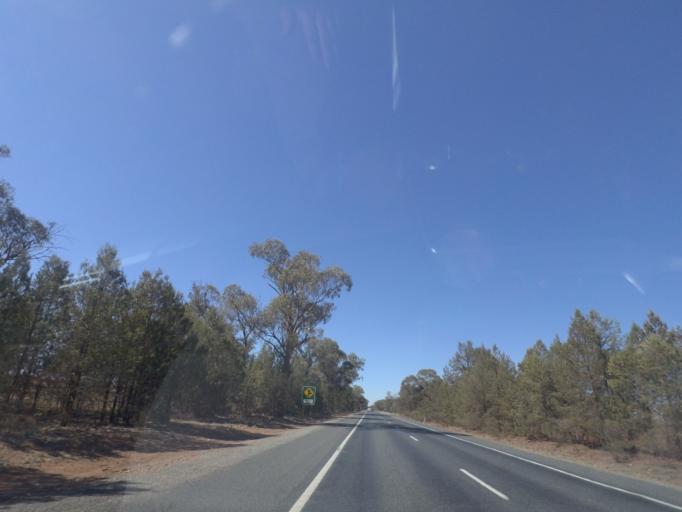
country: AU
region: New South Wales
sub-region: Bland
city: West Wyalong
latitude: -34.2129
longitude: 147.1083
